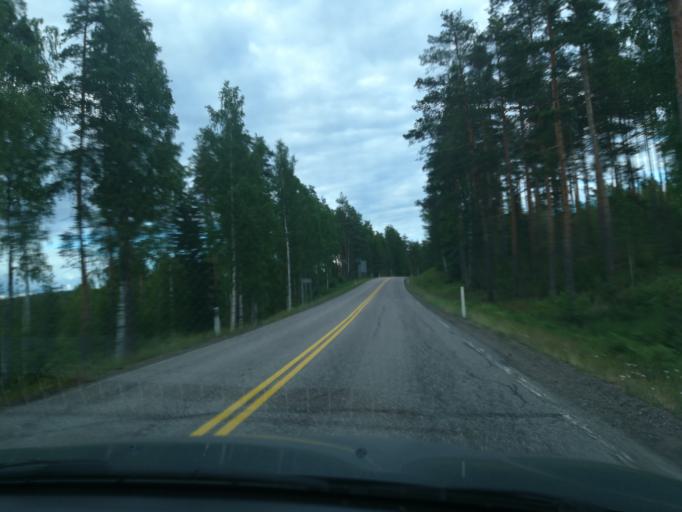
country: FI
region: South Karelia
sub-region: Lappeenranta
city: Savitaipale
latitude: 61.4998
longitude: 27.8333
